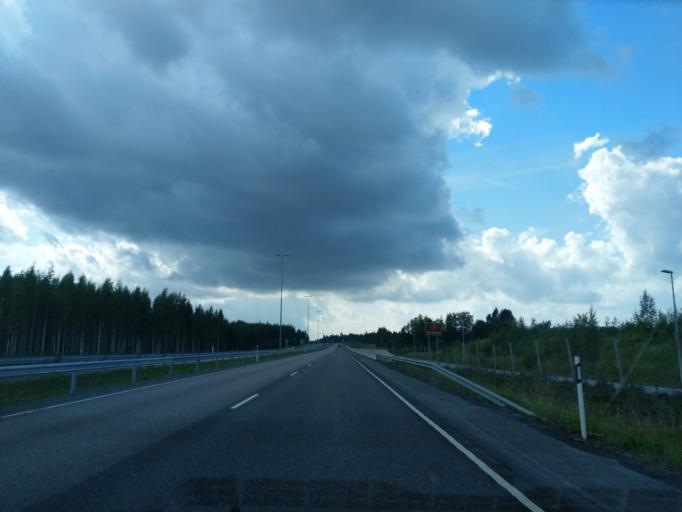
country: FI
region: South Karelia
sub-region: Imatra
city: Imatra
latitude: 61.1795
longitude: 28.7224
